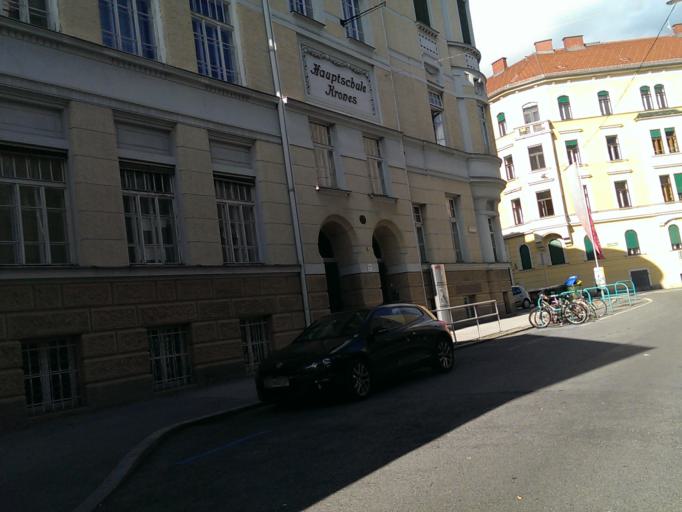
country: AT
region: Styria
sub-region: Graz Stadt
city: Graz
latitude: 47.0654
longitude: 15.4487
